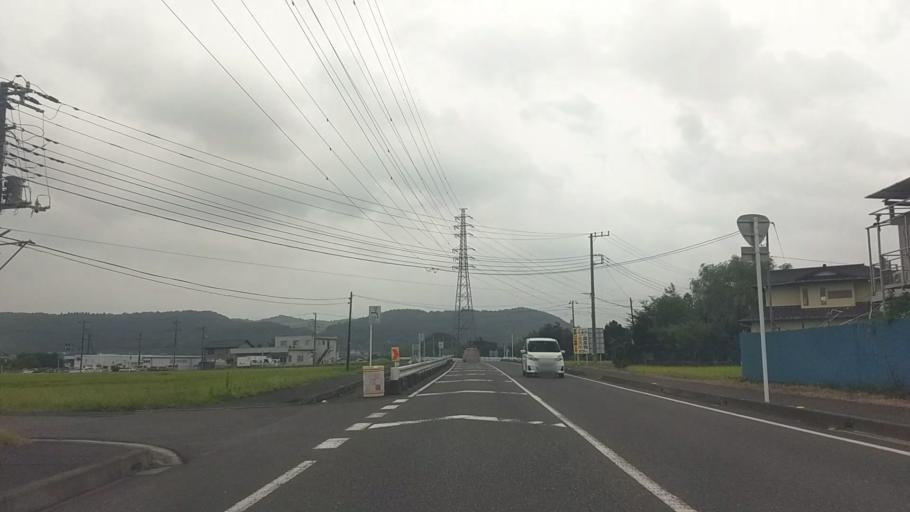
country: JP
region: Chiba
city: Kisarazu
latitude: 35.3115
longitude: 140.0604
